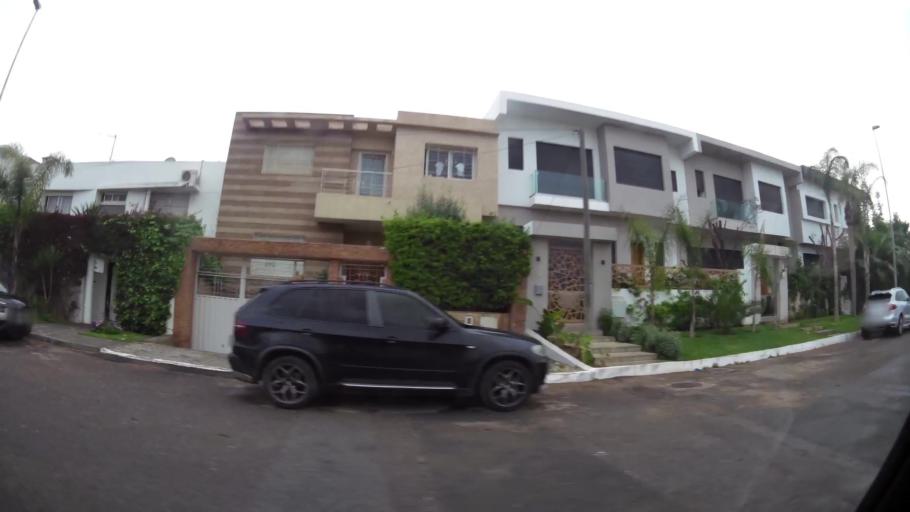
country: MA
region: Grand Casablanca
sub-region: Casablanca
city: Casablanca
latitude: 33.5816
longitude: -7.6772
